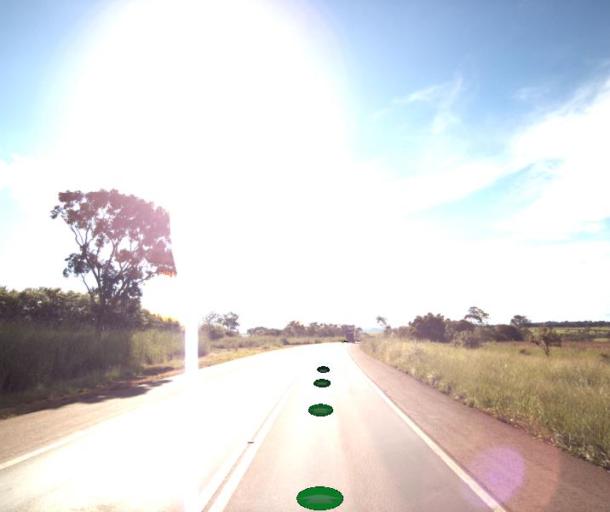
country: BR
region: Goias
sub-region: Rialma
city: Rialma
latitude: -15.3938
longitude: -49.5472
